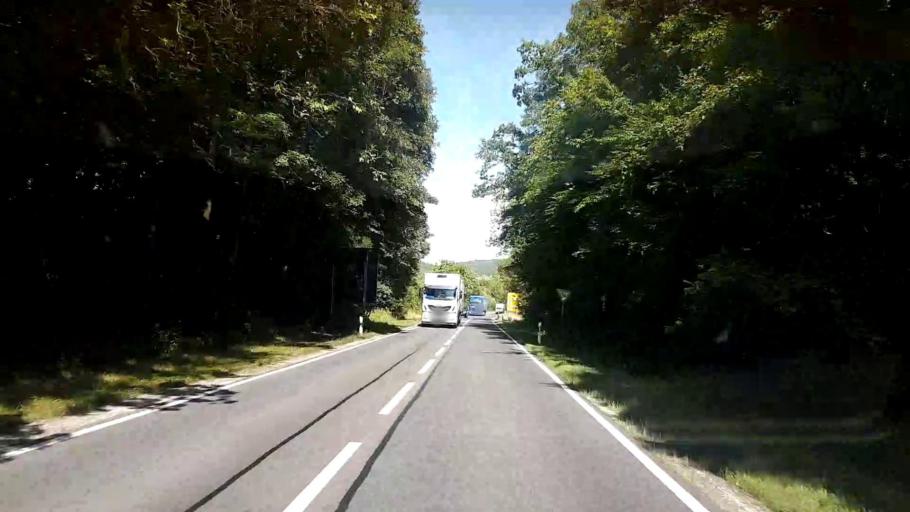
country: DE
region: Bavaria
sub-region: Upper Franconia
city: Ahorn
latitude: 50.2333
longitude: 10.9669
